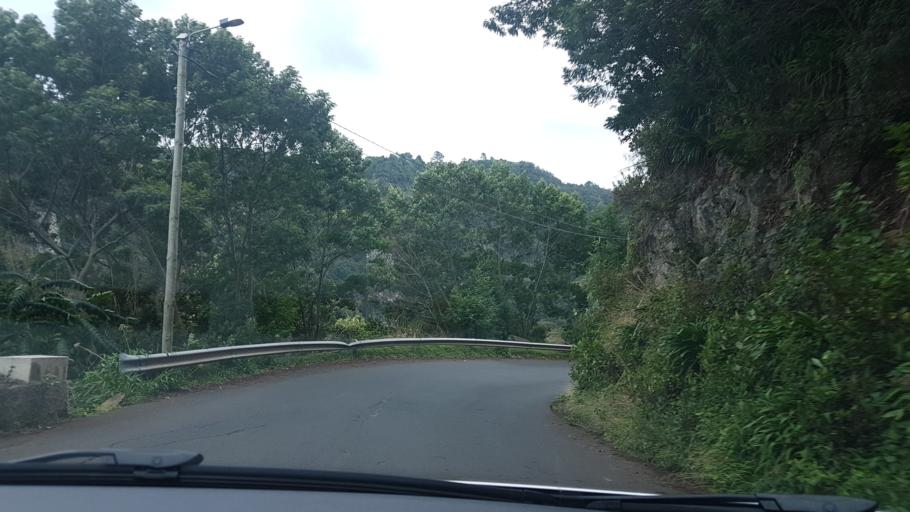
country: PT
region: Madeira
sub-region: Santana
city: Santana
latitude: 32.8229
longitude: -16.8996
